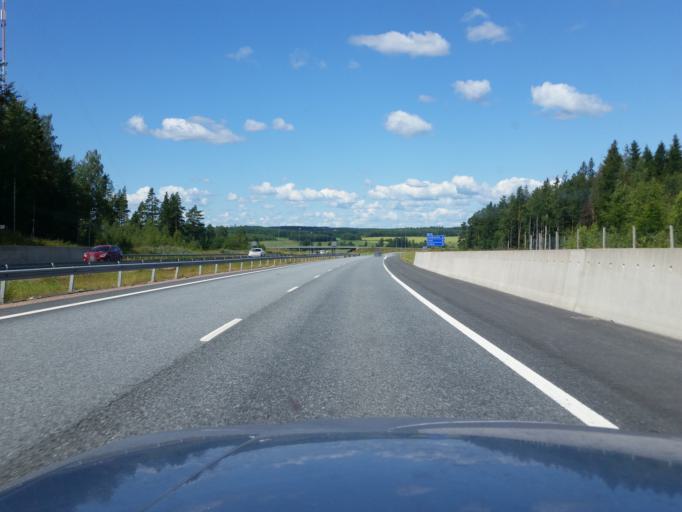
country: FI
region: Varsinais-Suomi
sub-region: Salo
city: Suomusjaervi
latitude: 60.3856
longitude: 23.5977
